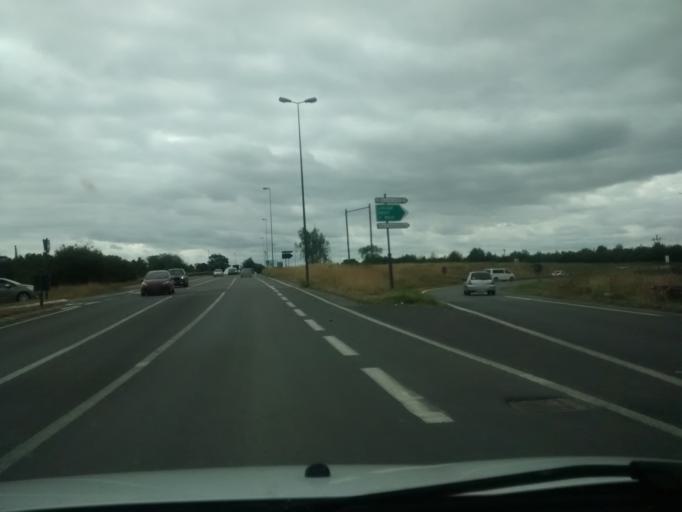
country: FR
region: Brittany
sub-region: Departement d'Ille-et-Vilaine
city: Saint-Jacques-de-la-Lande
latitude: 48.1030
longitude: -1.7140
